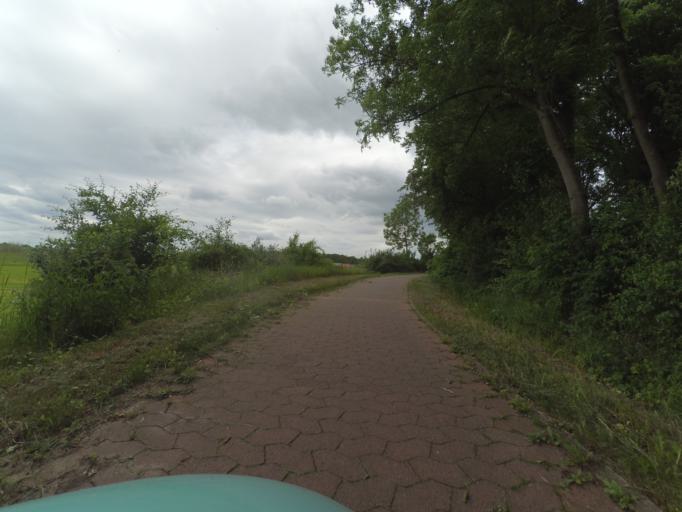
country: DE
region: Lower Saxony
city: Wunstorf
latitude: 52.4251
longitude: 9.4989
